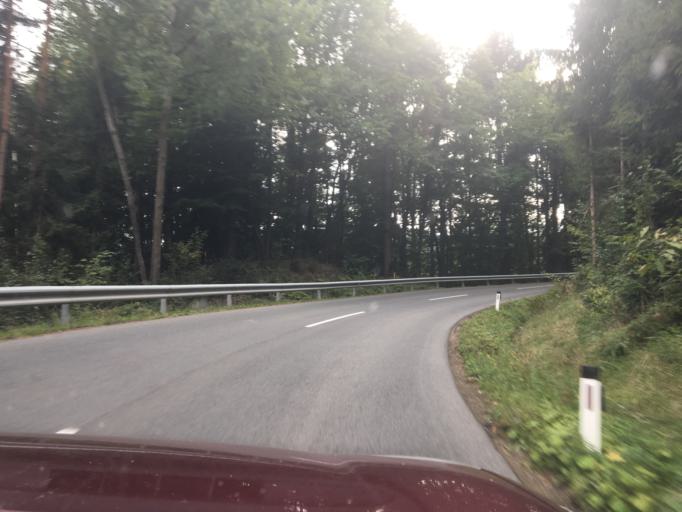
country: AT
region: Styria
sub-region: Politischer Bezirk Deutschlandsberg
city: Hollenegg
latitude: 46.8056
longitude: 15.1988
